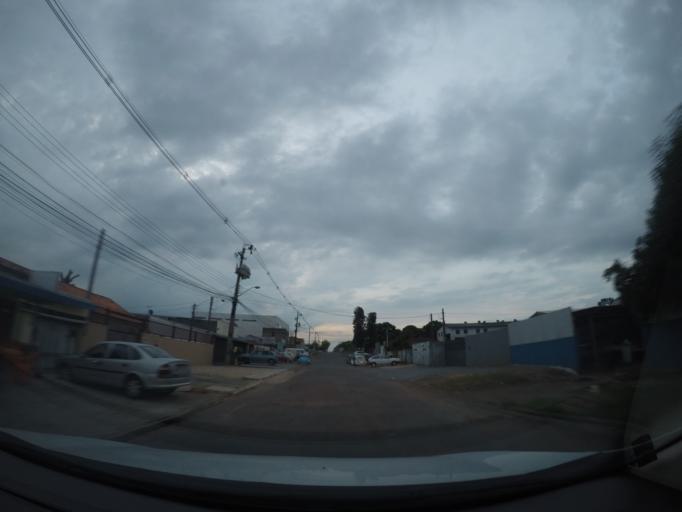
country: BR
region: Parana
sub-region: Sao Jose Dos Pinhais
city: Sao Jose dos Pinhais
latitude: -25.5125
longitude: -49.2239
